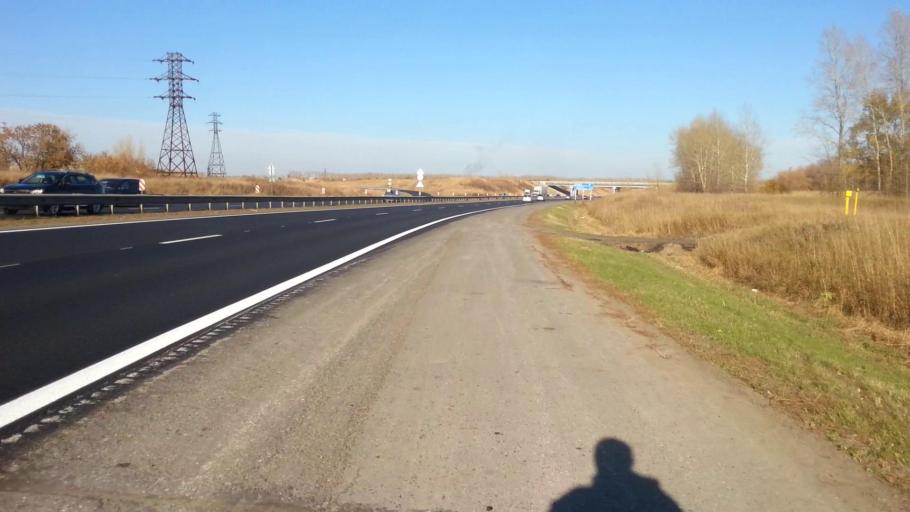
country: RU
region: Altai Krai
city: Novoaltaysk
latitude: 53.3682
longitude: 83.9501
